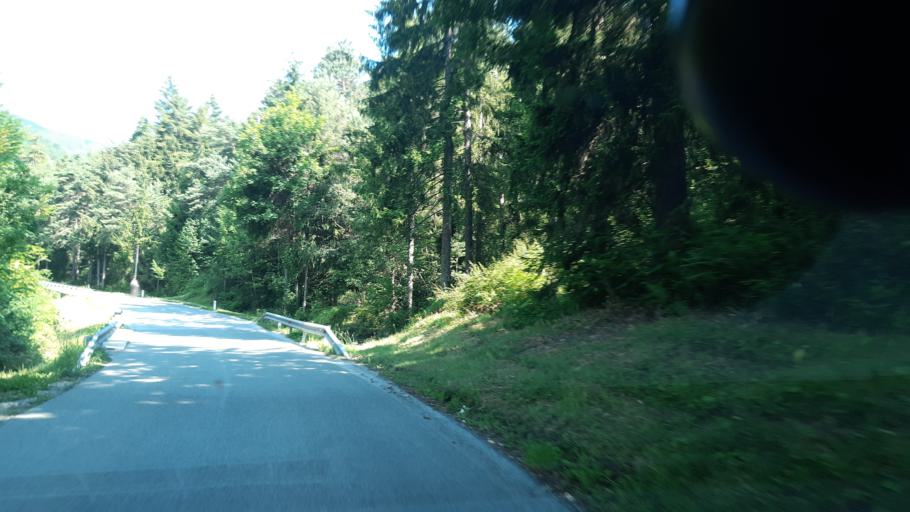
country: SI
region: Trzic
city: Bistrica pri Trzicu
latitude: 46.3610
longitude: 14.2865
